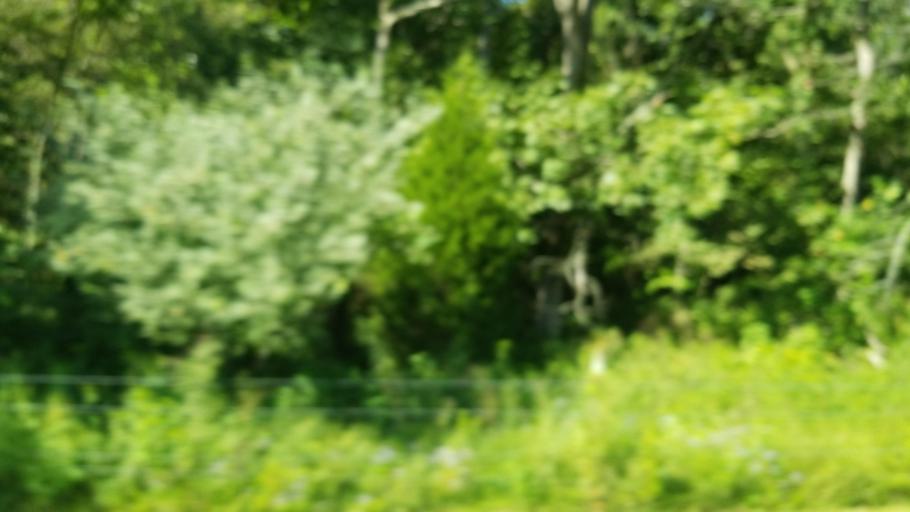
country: US
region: Illinois
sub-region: Saline County
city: Carrier Mills
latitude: 37.8015
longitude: -88.7169
